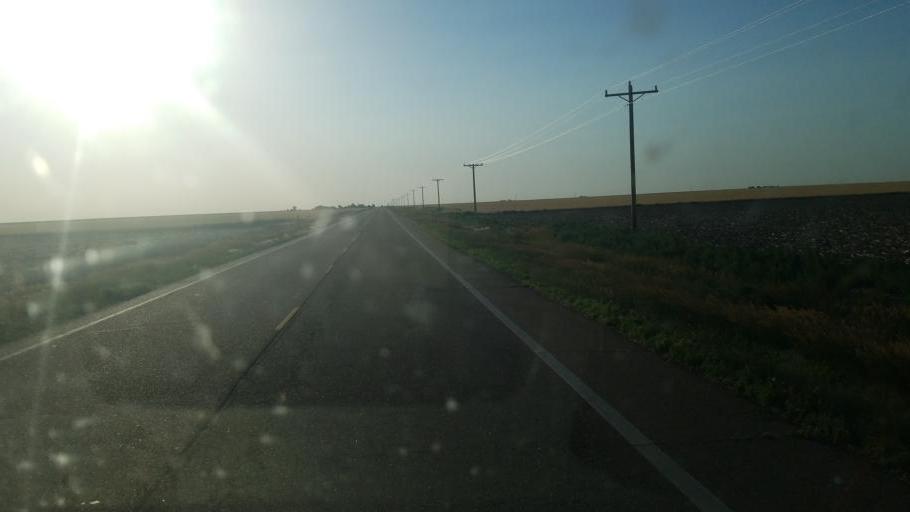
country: US
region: Kansas
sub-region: Gray County
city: Cimarron
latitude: 38.0592
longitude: -100.4923
